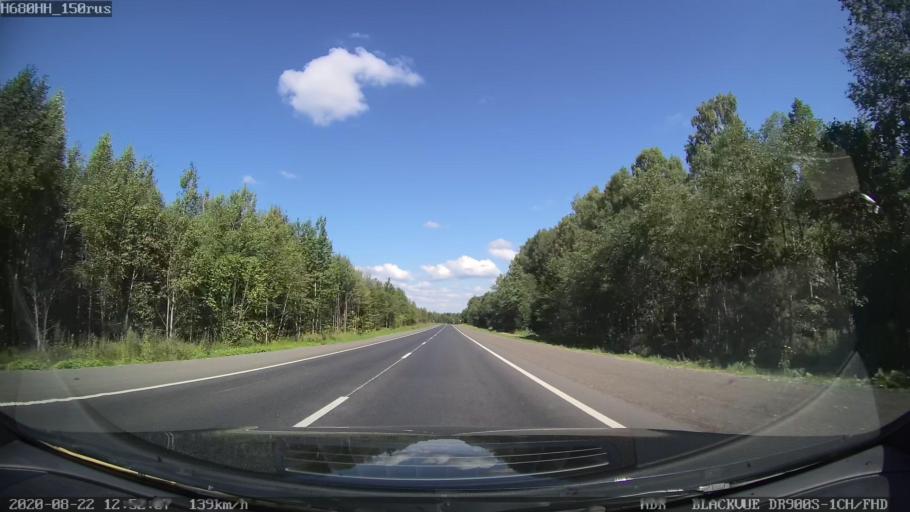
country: RU
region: Tverskaya
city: Rameshki
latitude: 57.4967
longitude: 36.2561
